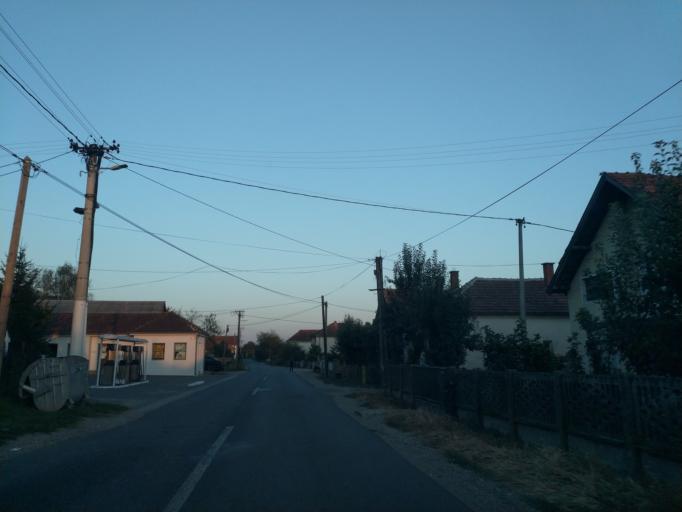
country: RS
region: Central Serbia
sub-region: Rasinski Okrug
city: Krusevac
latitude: 43.6046
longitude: 21.2426
